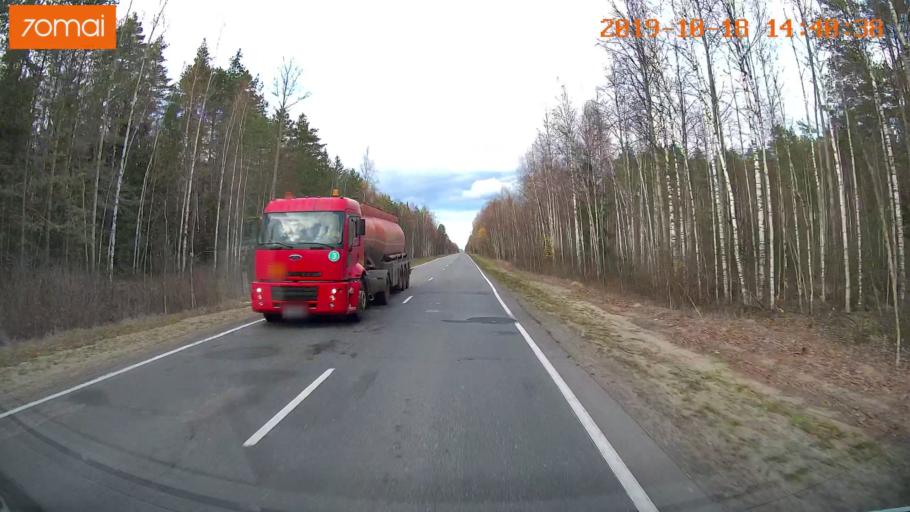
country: RU
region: Vladimir
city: Velikodvorskiy
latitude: 55.2796
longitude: 40.6694
